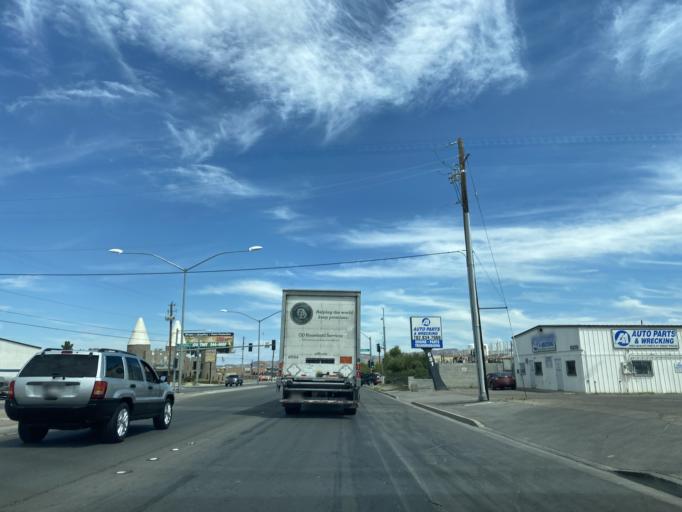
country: US
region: Nevada
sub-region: Clark County
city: Henderson
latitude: 36.0638
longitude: -115.0215
